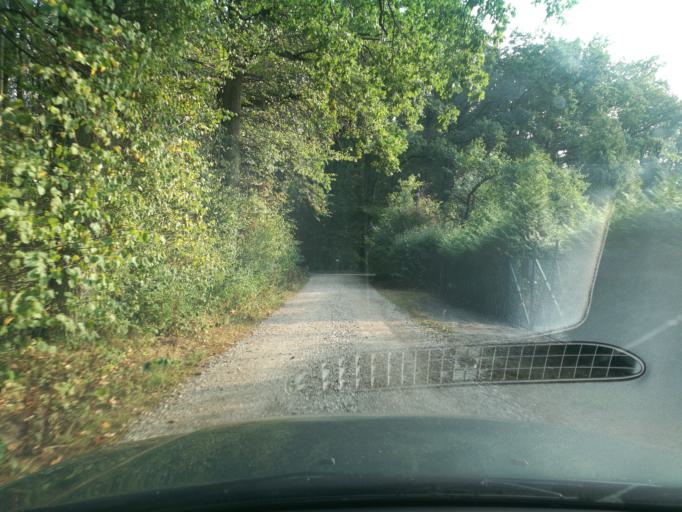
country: DE
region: Bavaria
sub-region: Regierungsbezirk Mittelfranken
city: Wetzendorf
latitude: 49.5186
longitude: 11.0662
